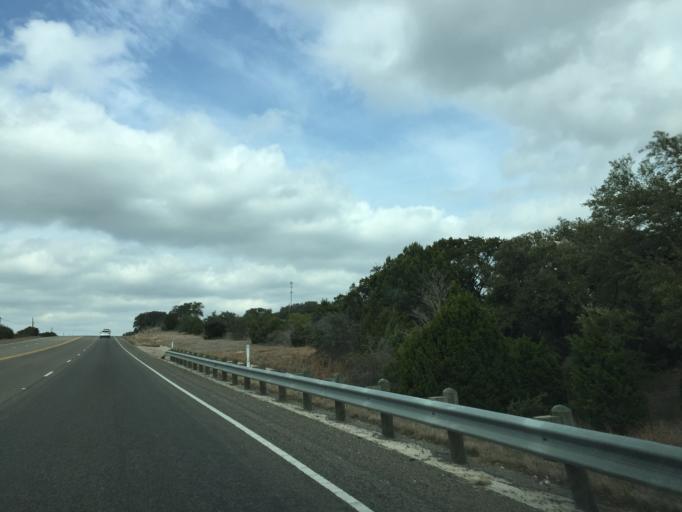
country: US
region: Texas
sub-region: Travis County
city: Briarcliff
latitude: 30.4267
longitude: -98.1347
